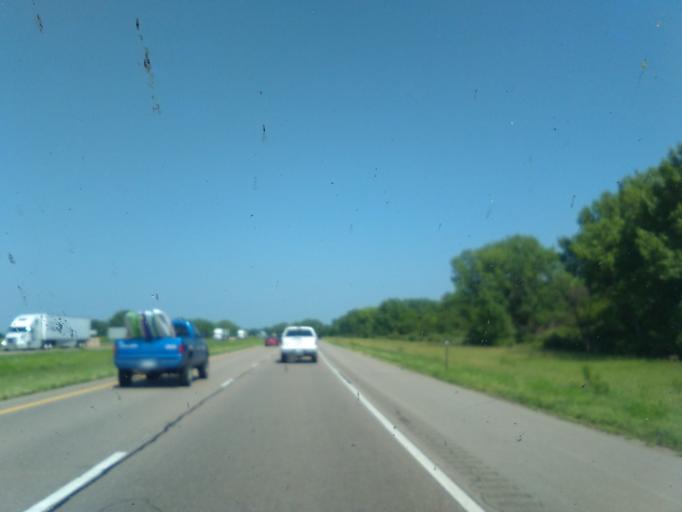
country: US
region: Nebraska
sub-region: Buffalo County
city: Gibbon
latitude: 40.6907
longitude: -98.9284
